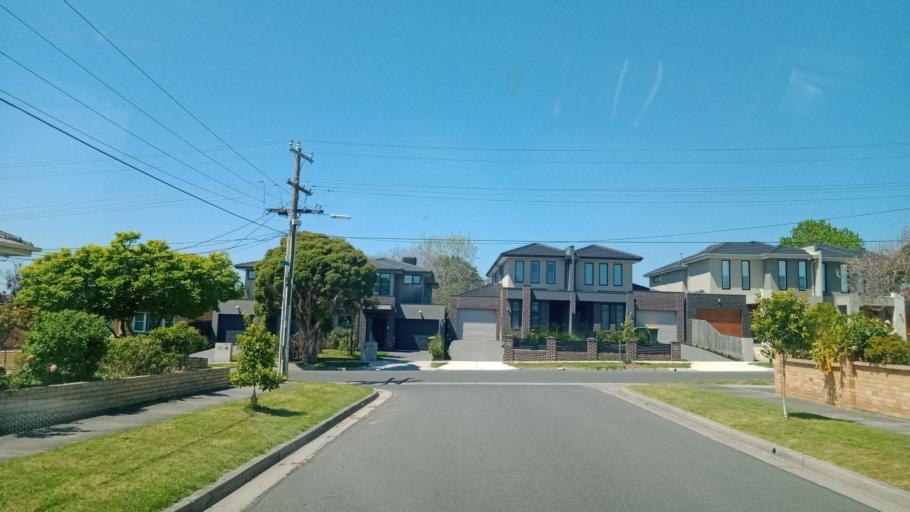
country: AU
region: Victoria
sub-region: Monash
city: Oakleigh South
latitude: -37.9240
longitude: 145.0748
